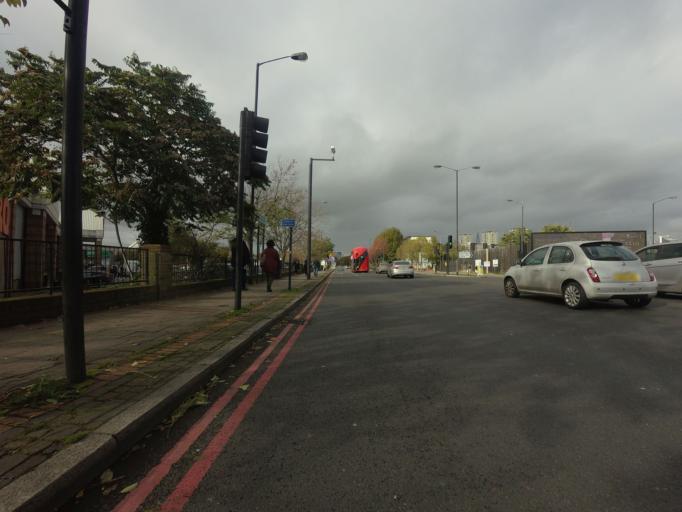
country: GB
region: England
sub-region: Greater London
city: Camberwell
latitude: 51.4839
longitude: -0.0662
